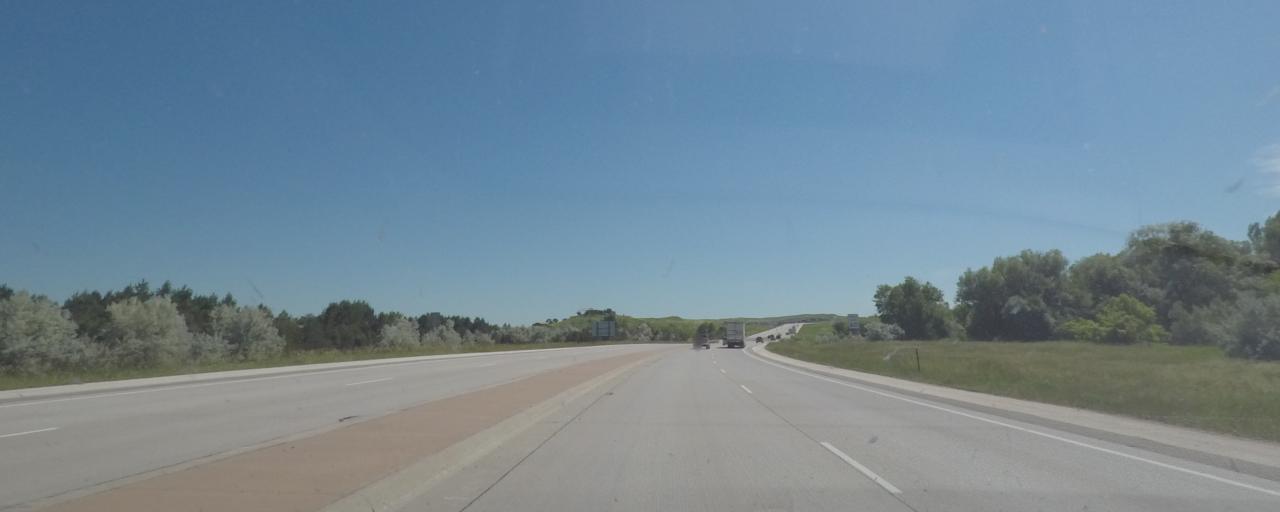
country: US
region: South Dakota
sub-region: Pennington County
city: Rapid Valley
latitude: 44.0575
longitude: -103.1651
